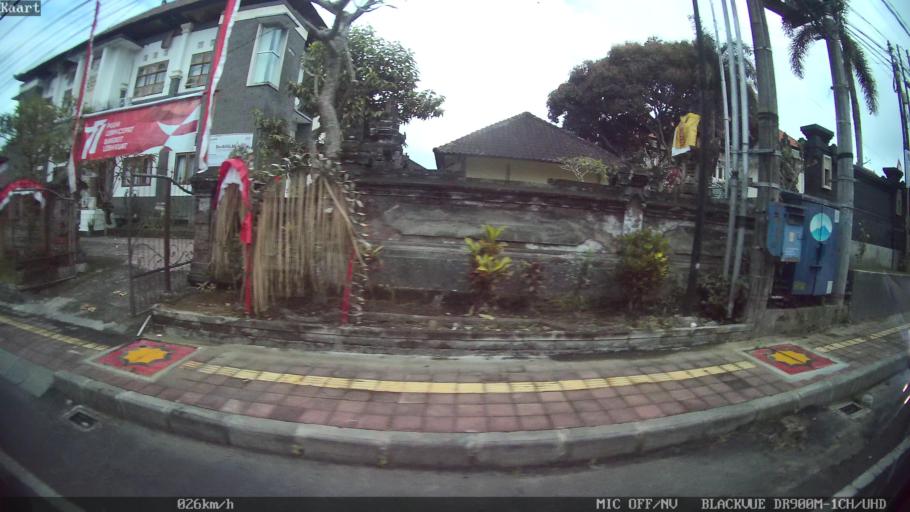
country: ID
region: Bali
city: Banjar Bebalang
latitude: -8.4680
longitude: 115.3526
